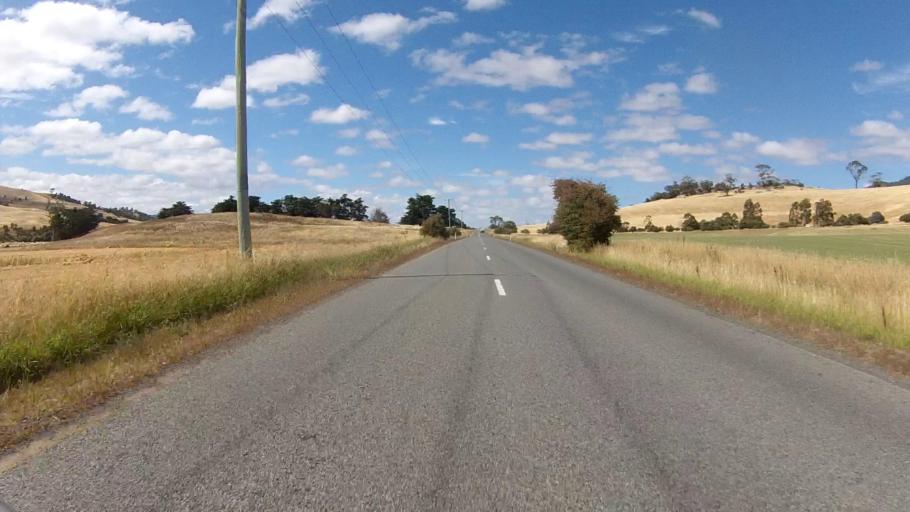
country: AU
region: Tasmania
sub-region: Brighton
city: Bridgewater
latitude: -42.5954
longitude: 147.4135
